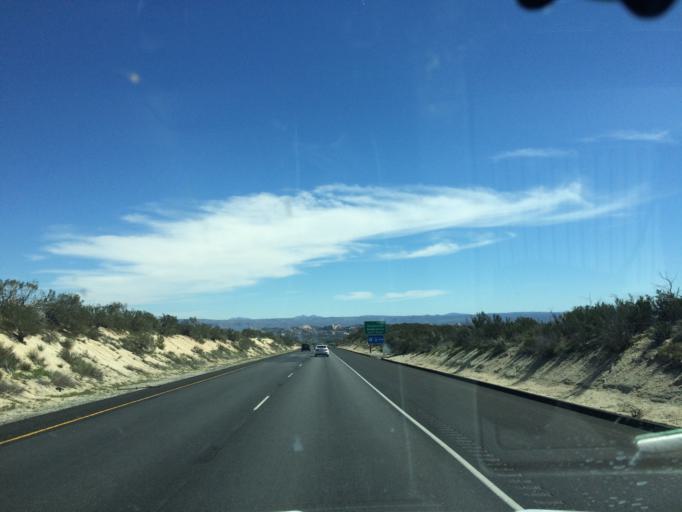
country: US
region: California
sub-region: San Diego County
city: Campo
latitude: 32.6883
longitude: -116.3062
